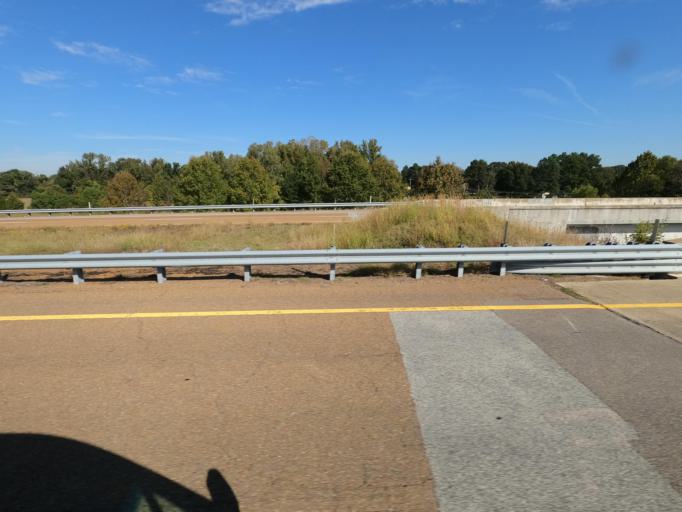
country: US
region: Tennessee
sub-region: Shelby County
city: Lakeland
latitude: 35.3101
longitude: -89.7629
